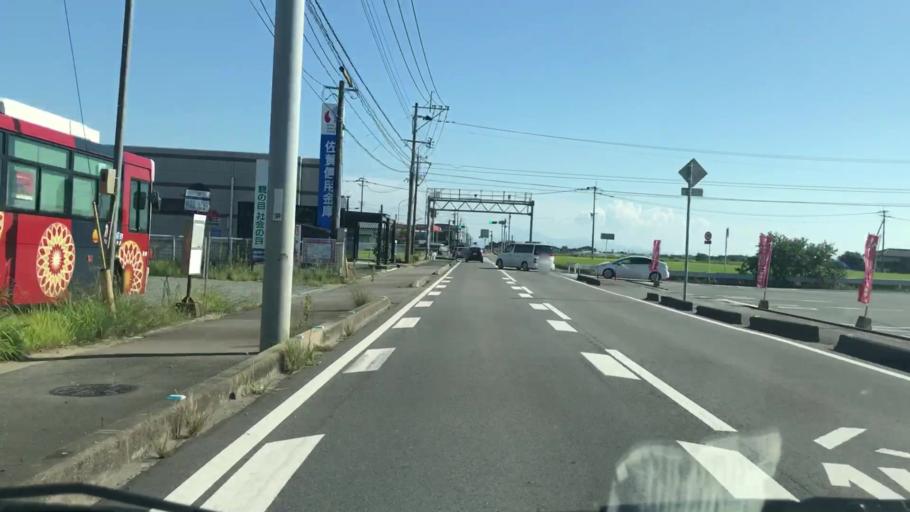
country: JP
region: Saga Prefecture
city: Okawa
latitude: 33.2056
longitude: 130.3353
